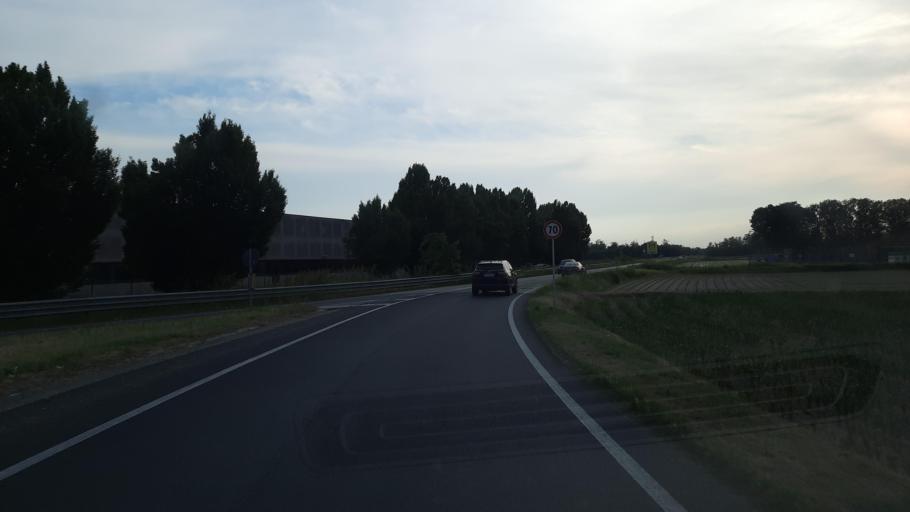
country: IT
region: Lombardy
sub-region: Provincia di Pavia
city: Villanova d'Ardenghi
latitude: 45.1627
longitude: 9.0377
